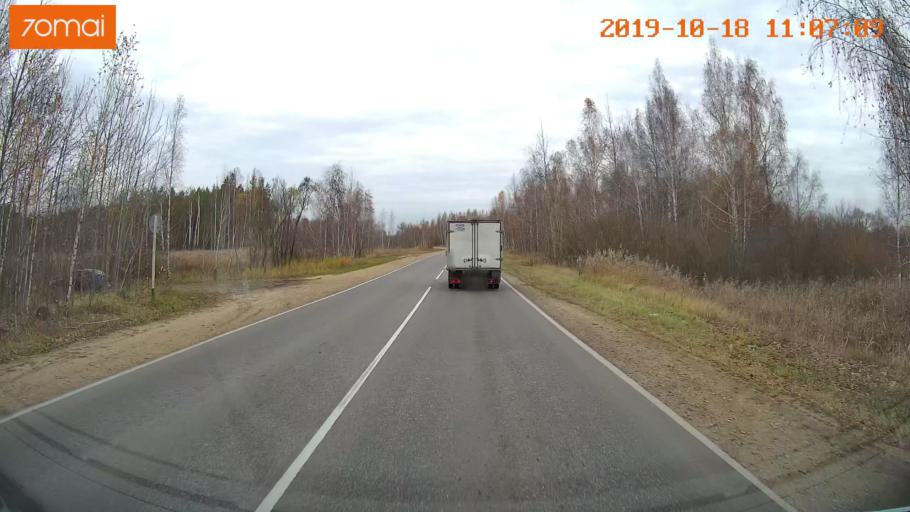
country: RU
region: Tula
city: Kimovsk
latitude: 53.9253
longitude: 38.5349
